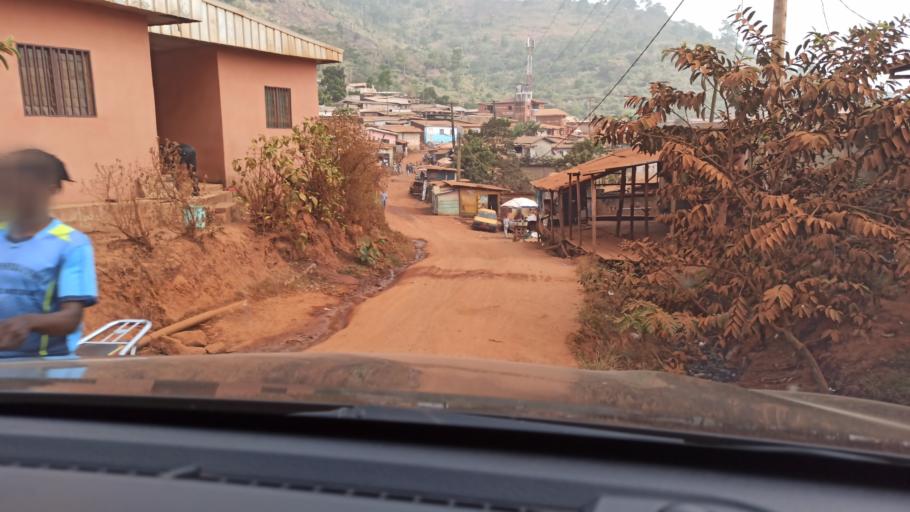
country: CM
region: Centre
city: Yaounde
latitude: 3.8798
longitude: 11.4795
